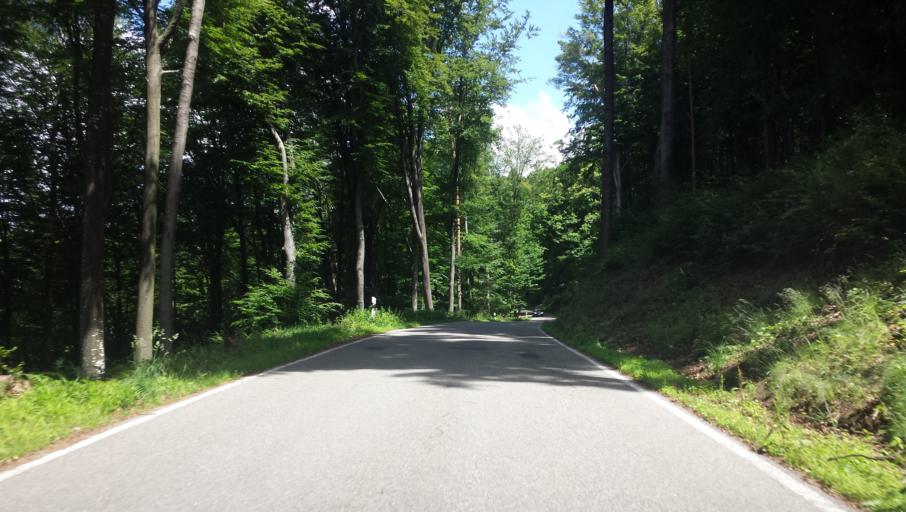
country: DE
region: Rheinland-Pfalz
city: Waldhambach
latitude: 49.1834
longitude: 7.9798
